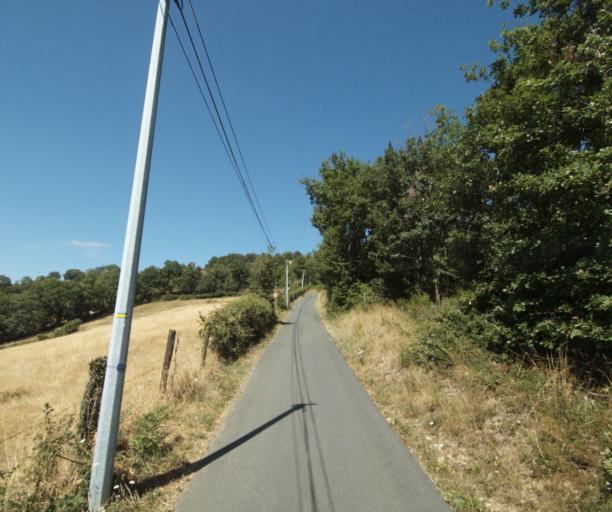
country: FR
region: Rhone-Alpes
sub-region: Departement du Rhone
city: Montrottier
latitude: 45.8037
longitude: 4.5099
